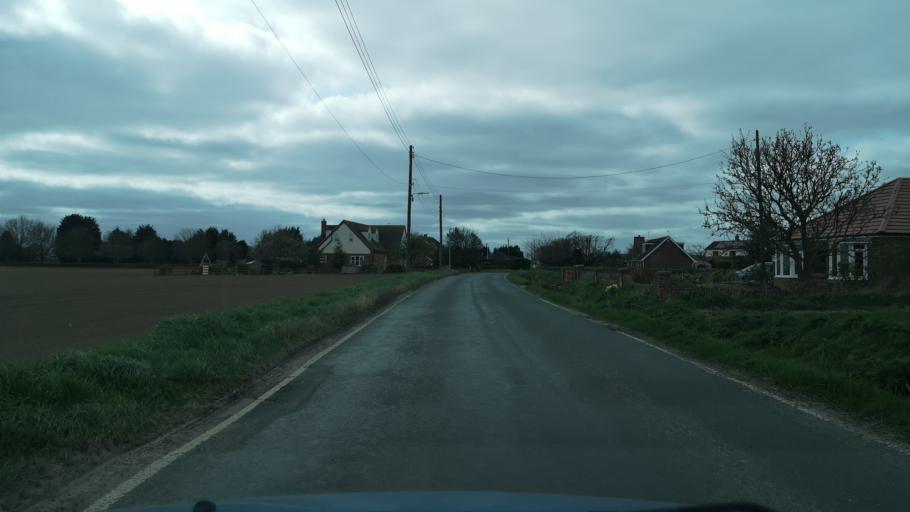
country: GB
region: England
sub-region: East Riding of Yorkshire
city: Skelton
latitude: 53.6939
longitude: -0.8230
